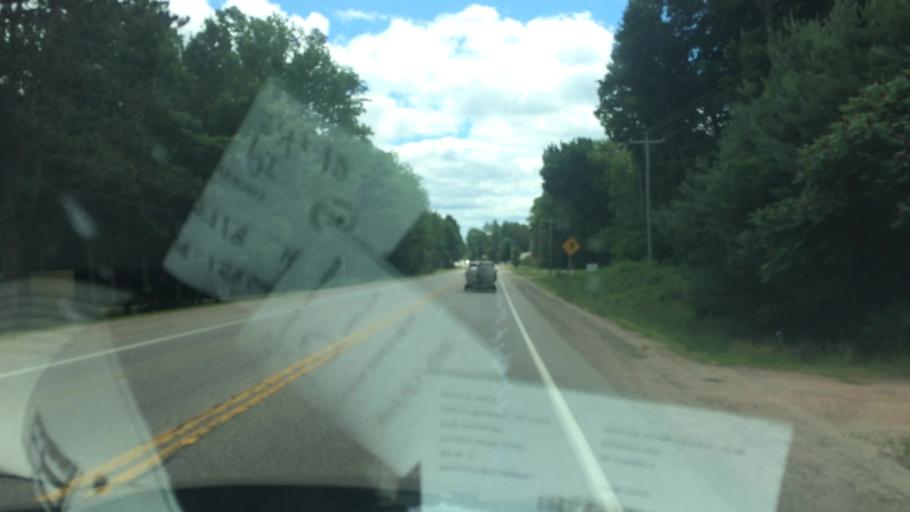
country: US
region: Wisconsin
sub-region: Vilas County
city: Eagle River
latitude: 45.8041
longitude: -89.3199
